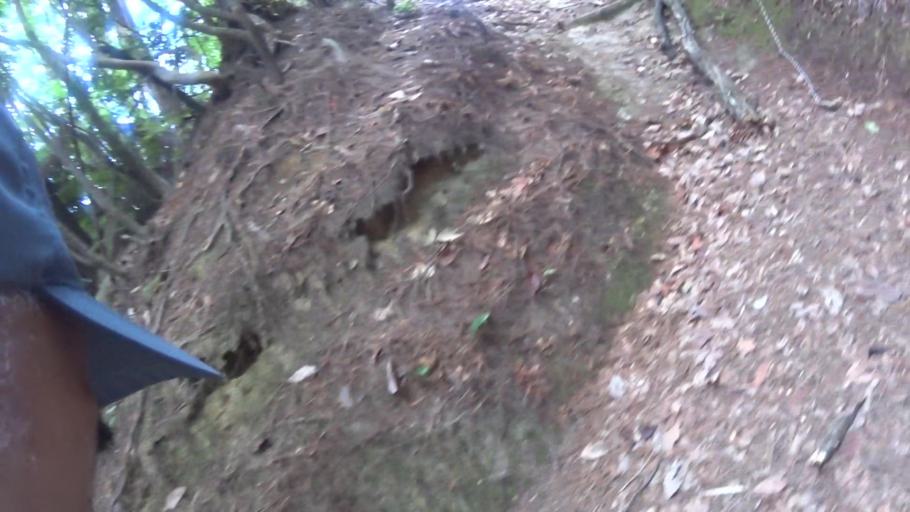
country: JP
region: Nara
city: Yoshino-cho
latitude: 34.3613
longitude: 135.8705
